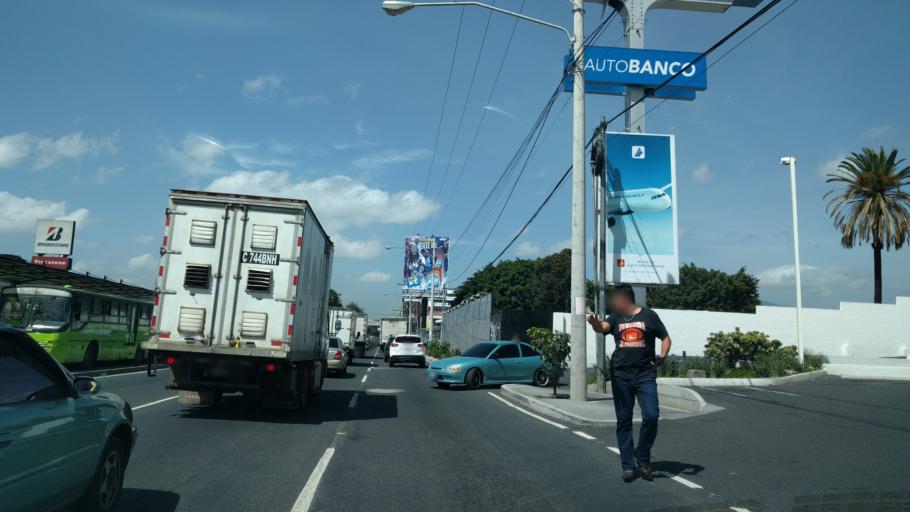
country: GT
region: Guatemala
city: Mixco
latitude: 14.5930
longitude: -90.5589
